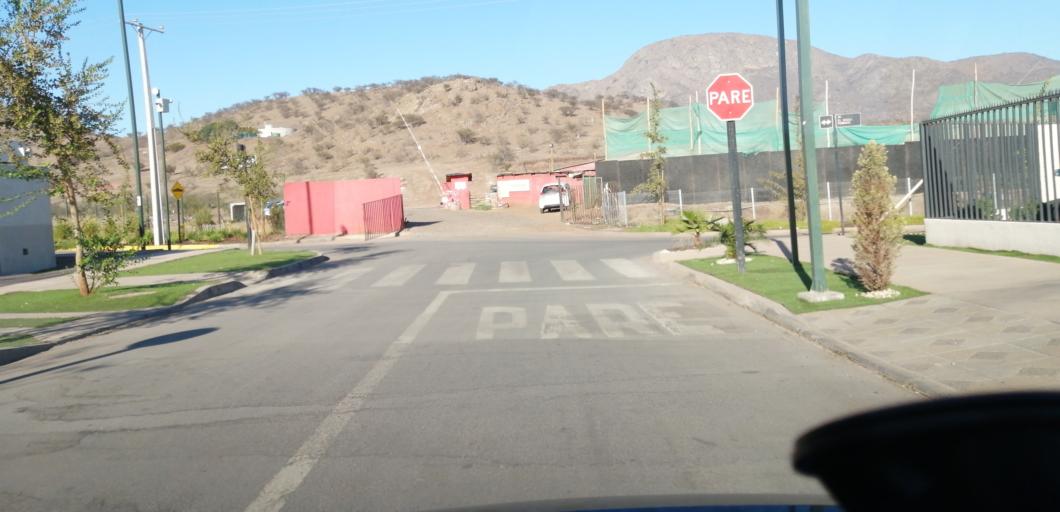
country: CL
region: Santiago Metropolitan
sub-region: Provincia de Santiago
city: Lo Prado
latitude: -33.4679
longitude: -70.8624
